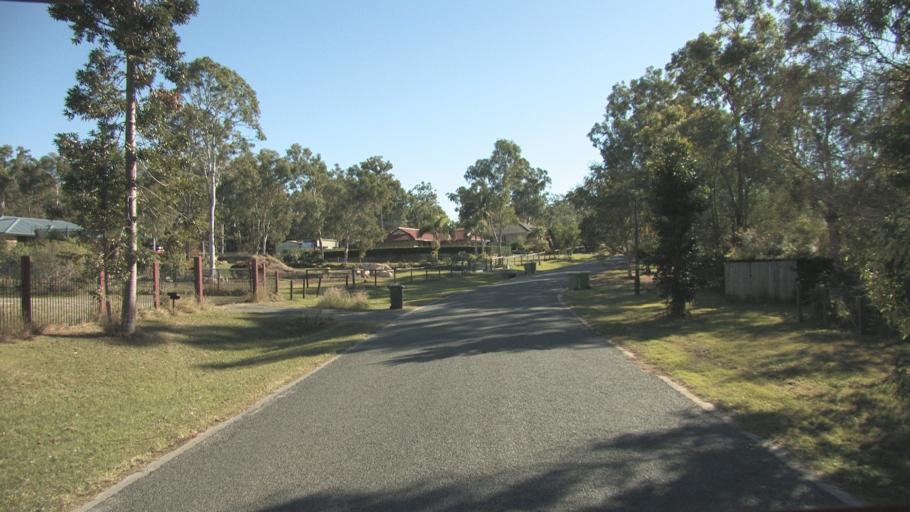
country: AU
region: Queensland
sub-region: Logan
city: North Maclean
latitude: -27.7453
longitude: 152.9578
